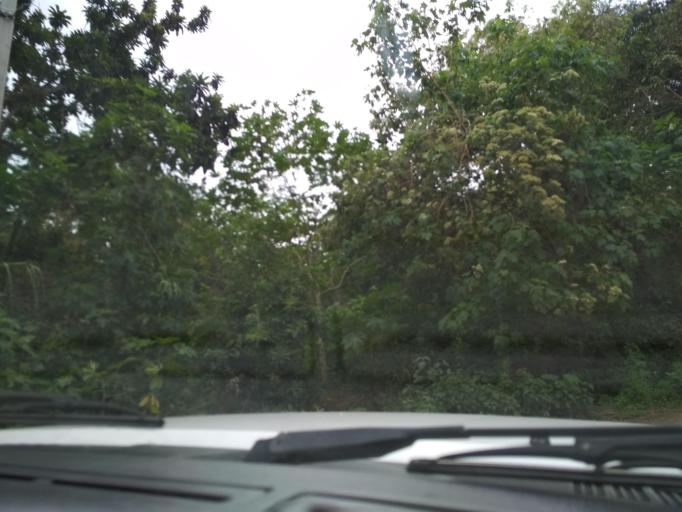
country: MX
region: Veracruz
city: El Castillo
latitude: 19.5840
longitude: -96.8701
